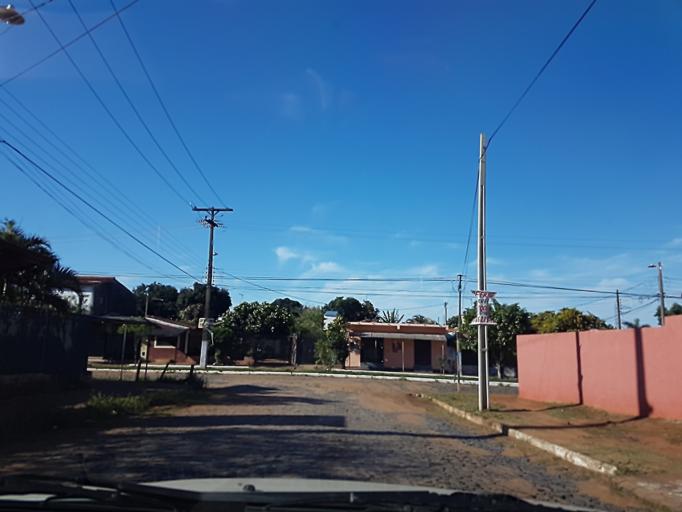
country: PY
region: Central
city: San Lorenzo
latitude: -25.2756
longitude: -57.4639
